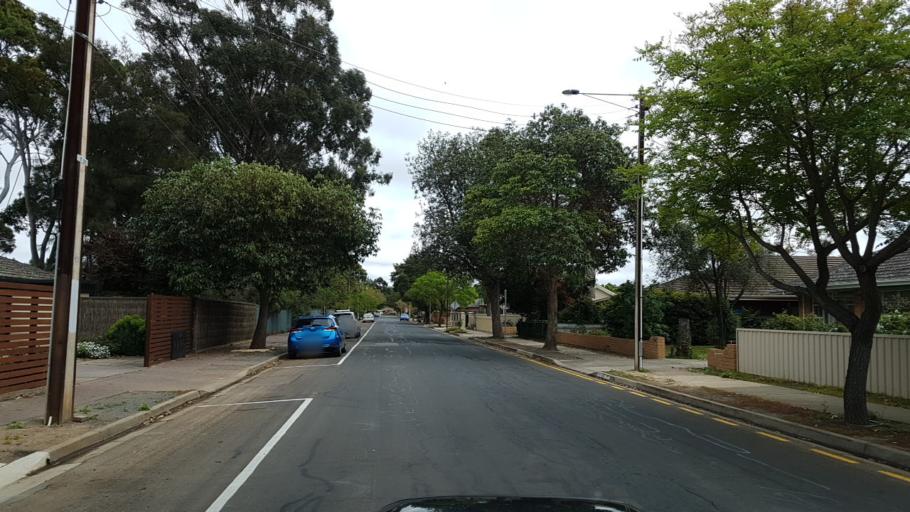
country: AU
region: South Australia
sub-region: Norwood Payneham St Peters
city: Marden
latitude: -34.8926
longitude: 138.6380
